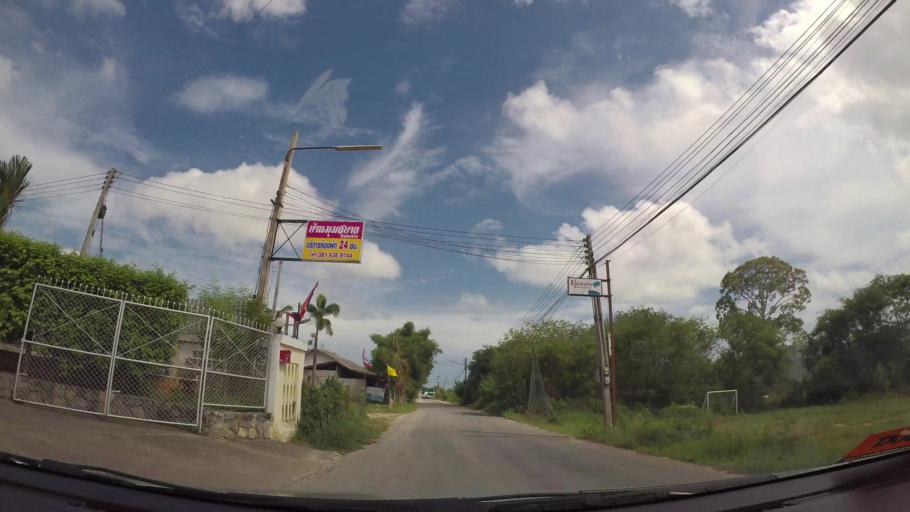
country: TH
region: Chon Buri
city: Sattahip
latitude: 12.6931
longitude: 100.9015
